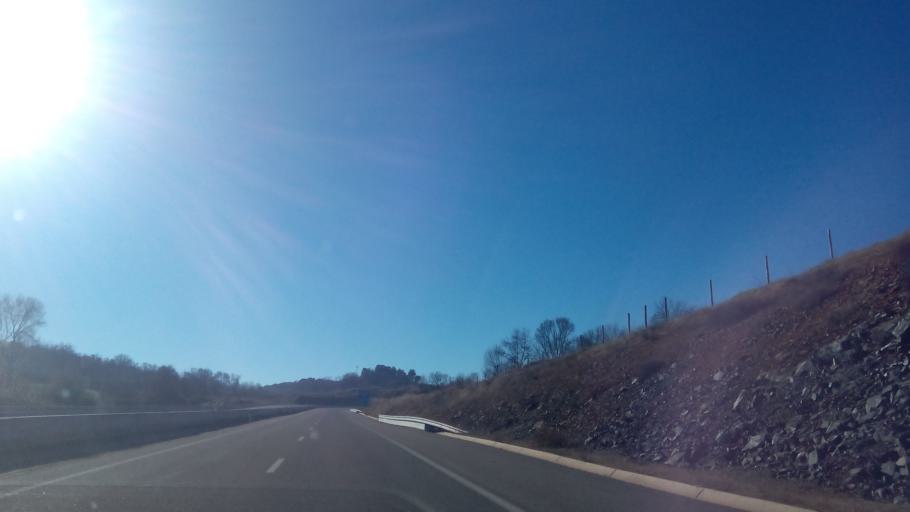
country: PT
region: Braganca
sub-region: Braganca Municipality
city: Braganca
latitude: 41.7782
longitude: -6.7467
